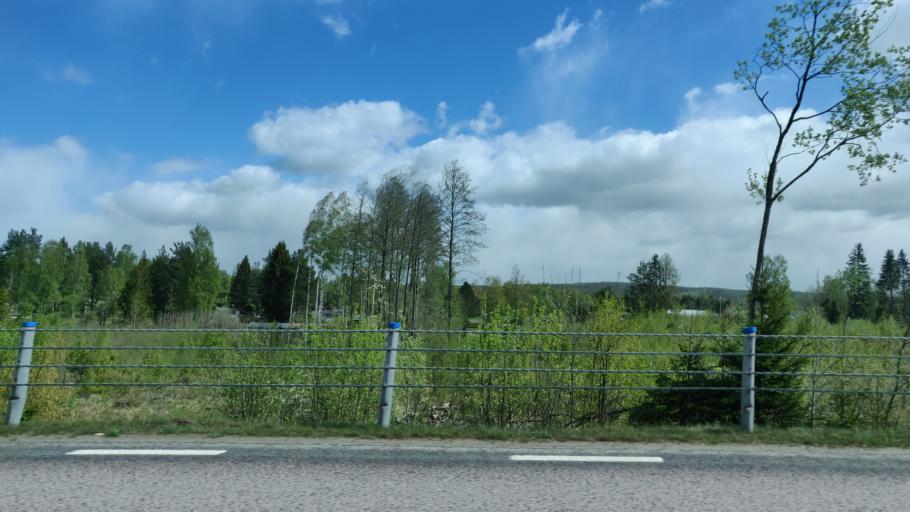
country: SE
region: Vaermland
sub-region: Karlstads Kommun
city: Skattkarr
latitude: 59.5212
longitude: 13.6173
